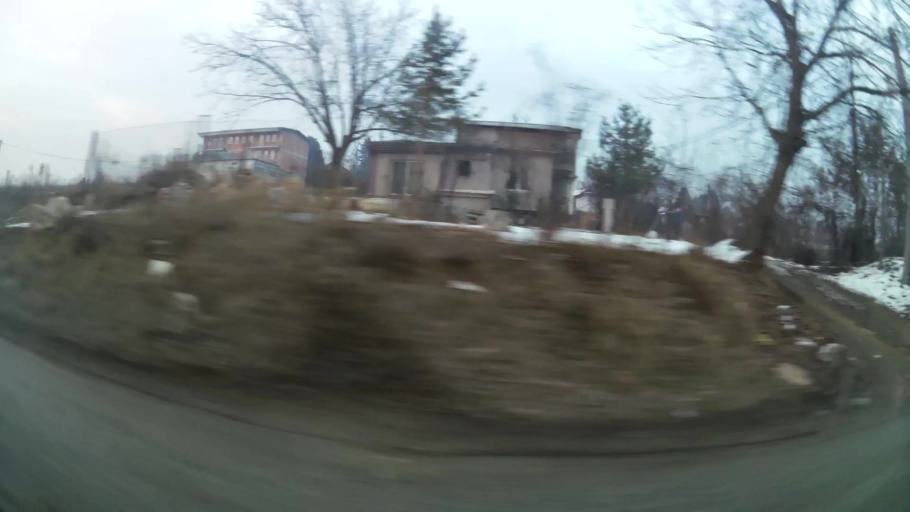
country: MK
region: Suto Orizari
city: Suto Orizare
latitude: 42.0289
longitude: 21.4080
